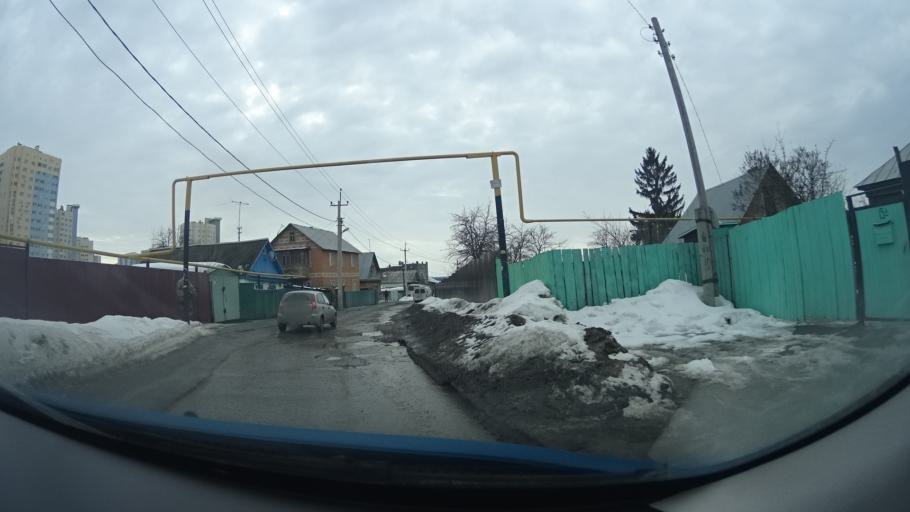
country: RU
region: Bashkortostan
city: Ufa
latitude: 54.6923
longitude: 55.9884
